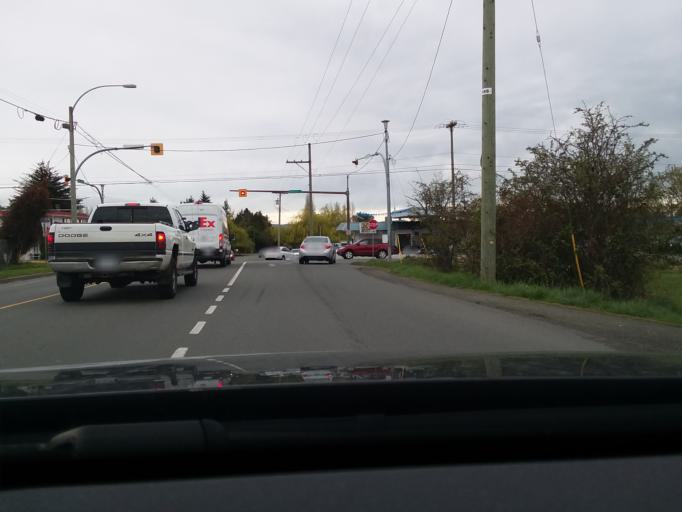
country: CA
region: British Columbia
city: North Saanich
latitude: 48.6296
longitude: -123.4203
